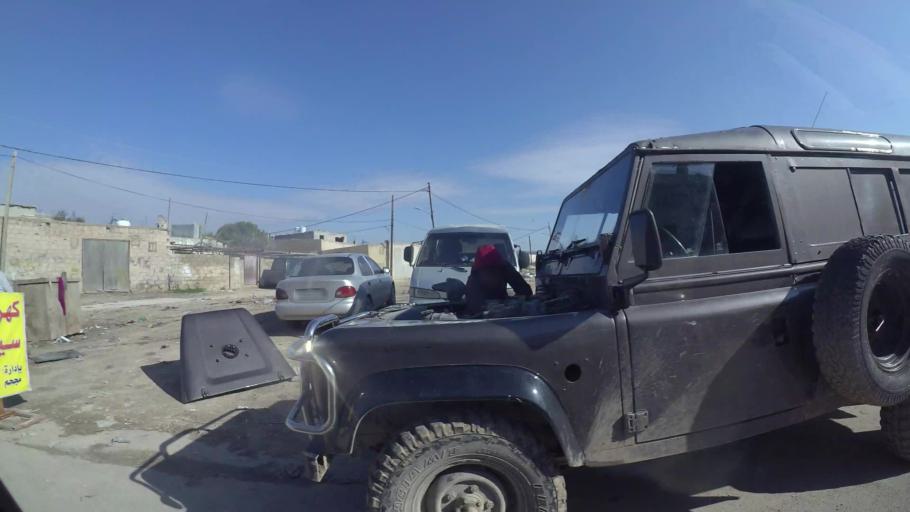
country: JO
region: Amman
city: Al Jubayhah
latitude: 32.0799
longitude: 35.8504
